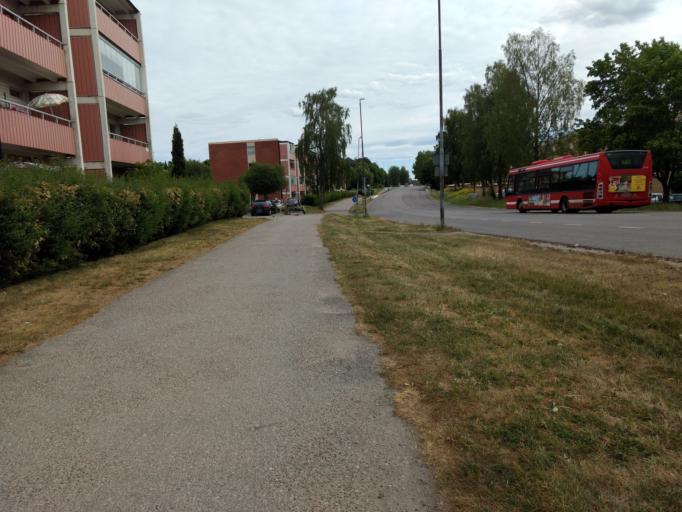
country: SE
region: Stockholm
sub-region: Upplands Vasby Kommun
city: Upplands Vaesby
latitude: 59.5237
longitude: 17.9164
